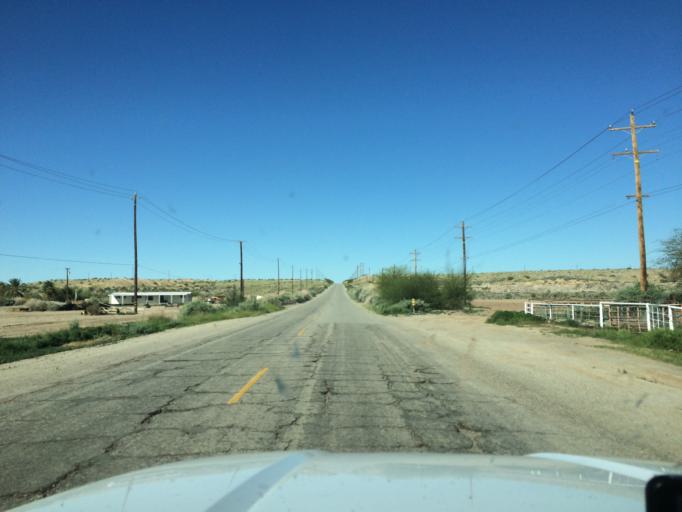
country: US
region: California
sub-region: Riverside County
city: Blythe
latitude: 33.6102
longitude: -114.6630
